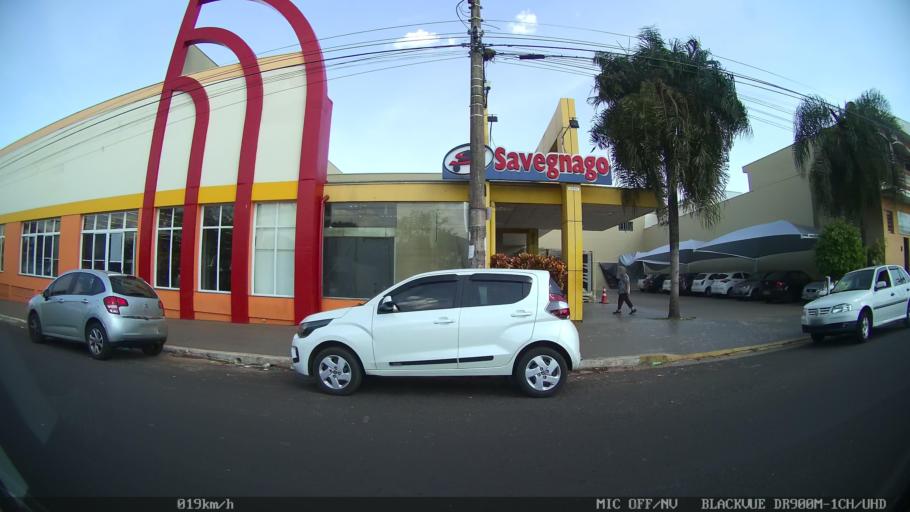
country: BR
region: Sao Paulo
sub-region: Ribeirao Preto
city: Ribeirao Preto
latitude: -21.1892
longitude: -47.8282
